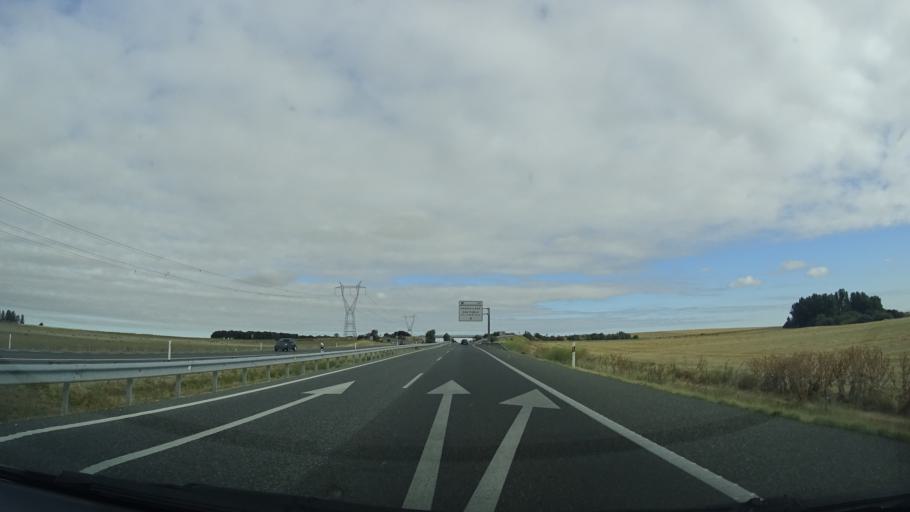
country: ES
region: Castille and Leon
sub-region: Provincia de Valladolid
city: San Pablo de la Moraleja
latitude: 41.1456
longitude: -4.7859
